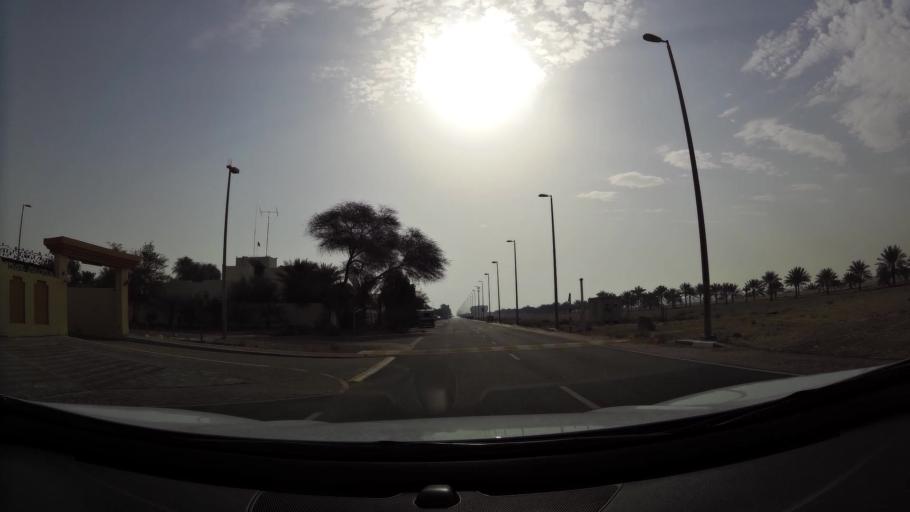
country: AE
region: Abu Dhabi
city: Abu Dhabi
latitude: 24.2421
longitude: 54.7125
